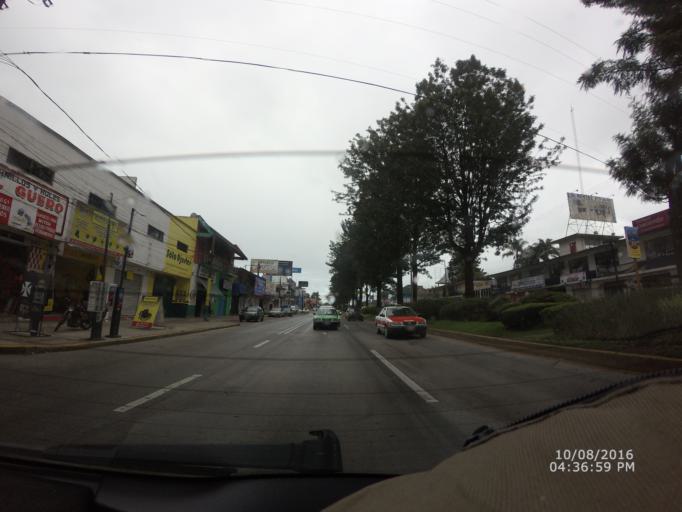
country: MX
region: Veracruz
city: Banderilla
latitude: 19.5614
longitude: -96.9261
